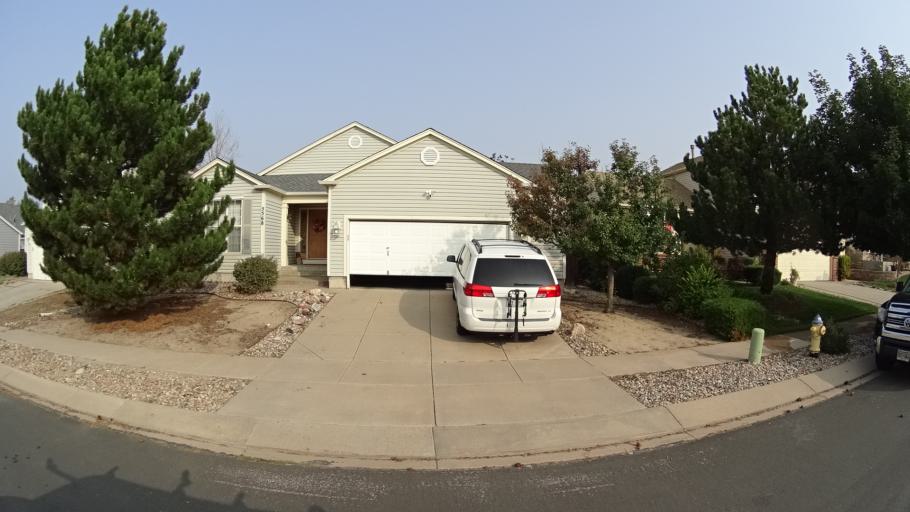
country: US
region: Colorado
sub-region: El Paso County
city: Cimarron Hills
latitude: 38.9316
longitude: -104.7277
